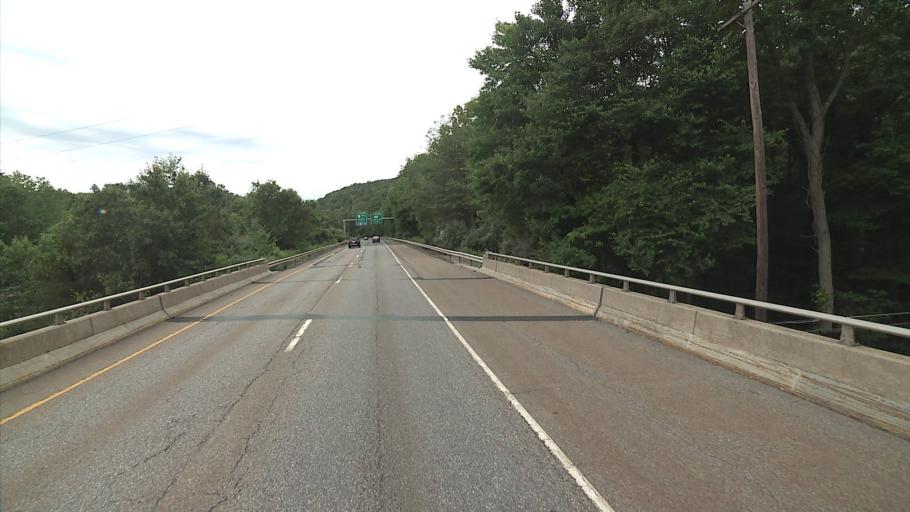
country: US
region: Connecticut
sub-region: Litchfield County
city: Thomaston
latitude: 41.6926
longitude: -73.0694
